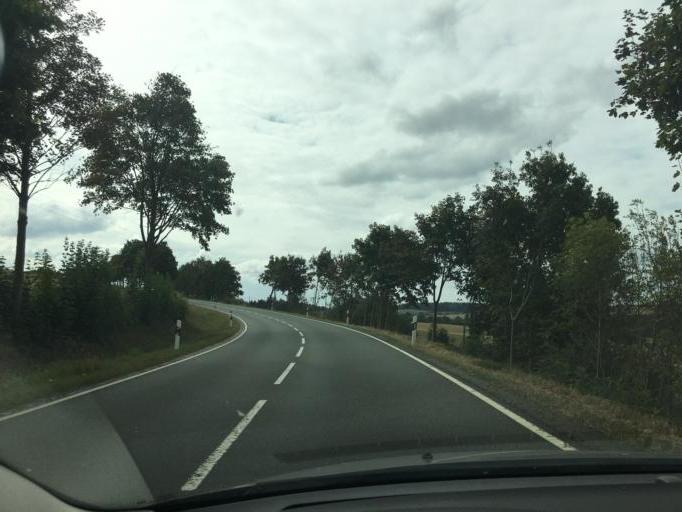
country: DE
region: Thuringia
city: Burgk
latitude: 50.5126
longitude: 11.7320
